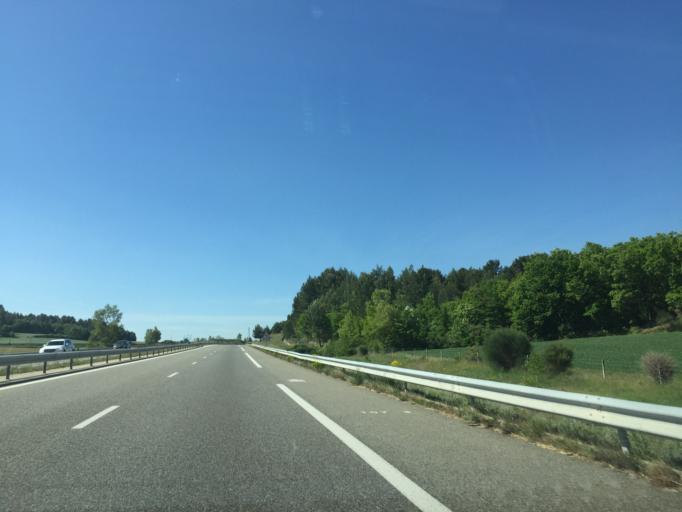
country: FR
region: Provence-Alpes-Cote d'Azur
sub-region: Departement des Alpes-de-Haute-Provence
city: Volonne
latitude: 44.0978
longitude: 5.9939
